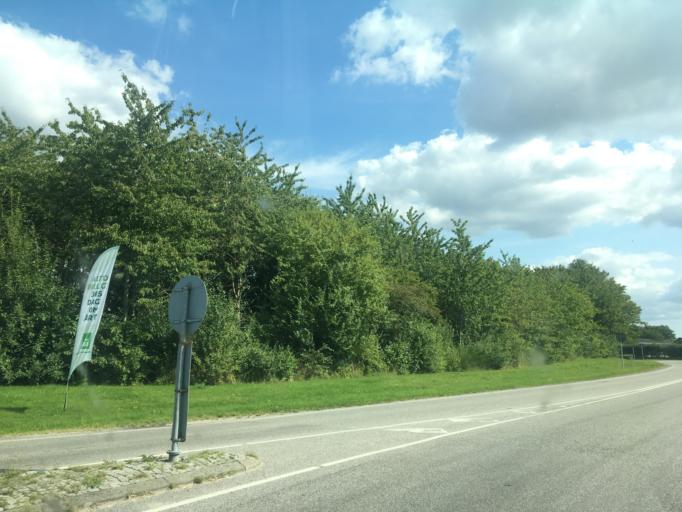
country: DK
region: South Denmark
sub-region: Middelfart Kommune
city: Ejby
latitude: 55.4010
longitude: 9.9744
